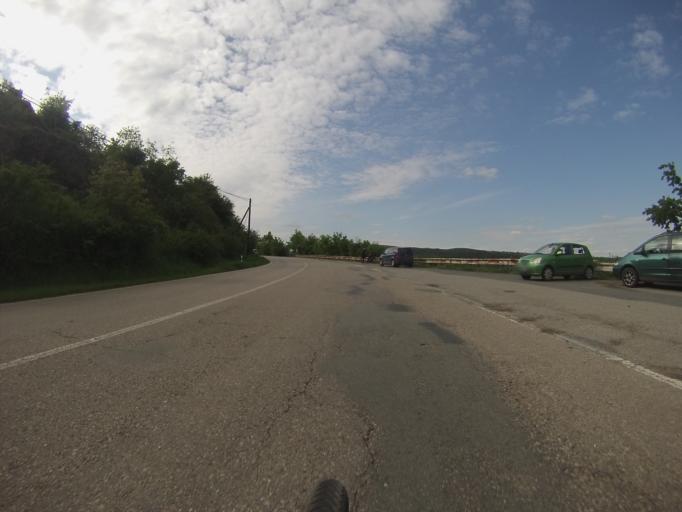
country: CZ
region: South Moravian
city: Troubsko
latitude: 49.2333
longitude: 16.5095
